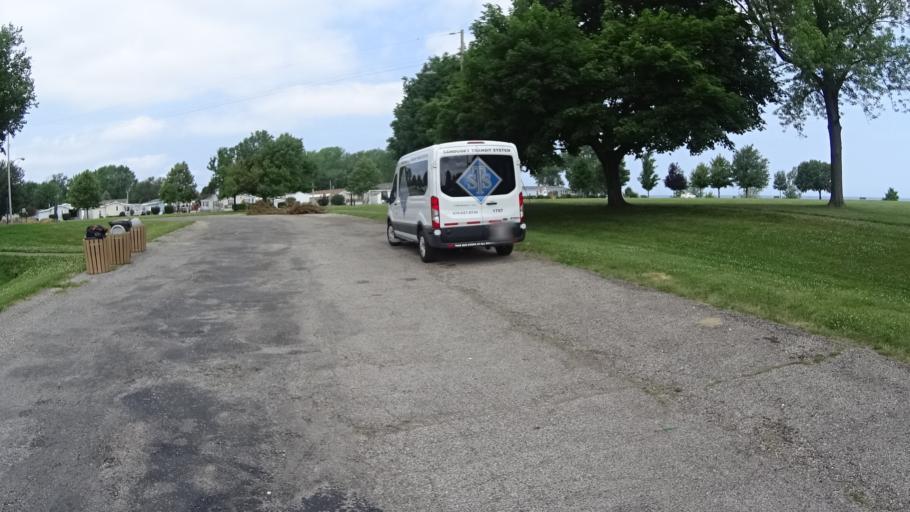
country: US
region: Ohio
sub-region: Lorain County
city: Vermilion
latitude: 41.4154
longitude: -82.3893
